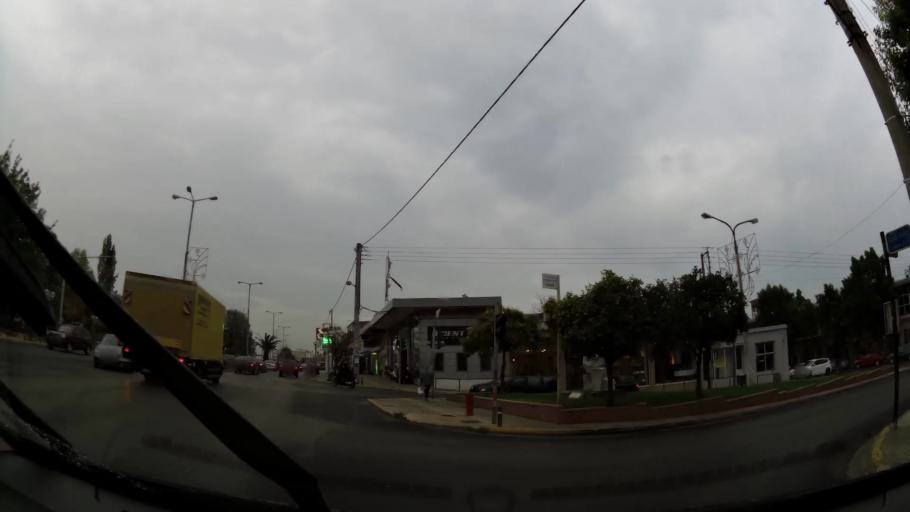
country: GR
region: Attica
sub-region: Nomarchia Athinas
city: Aigaleo
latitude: 37.9935
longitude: 23.6758
